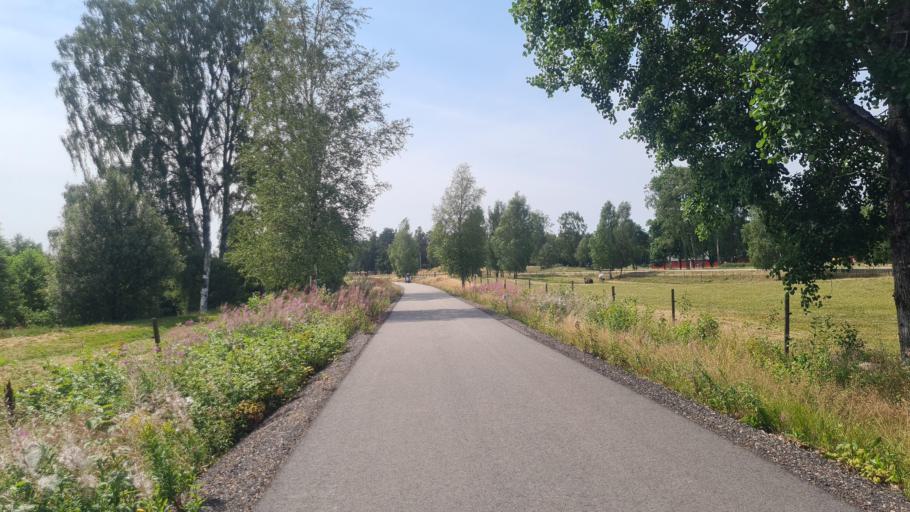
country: SE
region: Kronoberg
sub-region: Ljungby Kommun
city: Lagan
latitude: 56.8717
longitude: 13.9810
